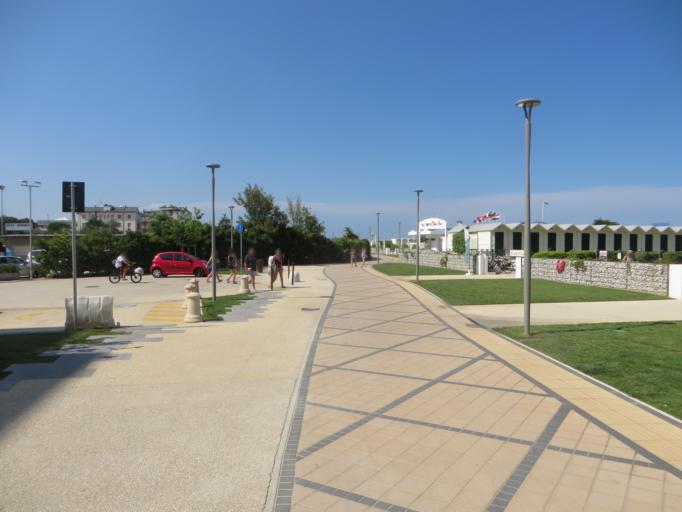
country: IT
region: Emilia-Romagna
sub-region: Provincia di Ravenna
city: Cervia
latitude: 44.2788
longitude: 12.3525
